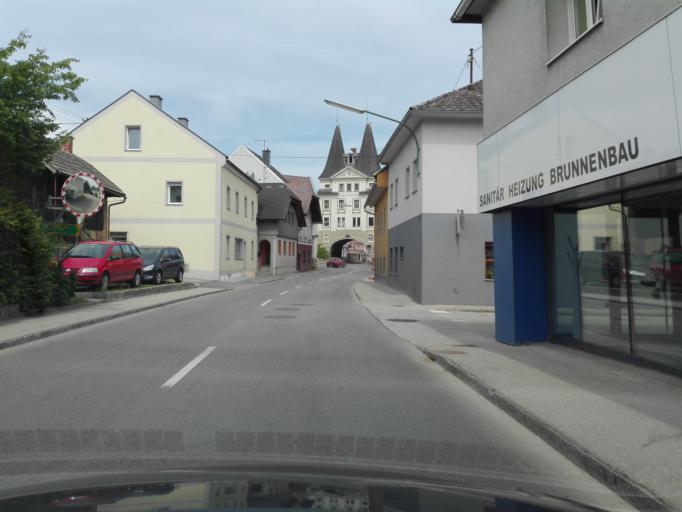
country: AT
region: Upper Austria
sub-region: Politischer Bezirk Vocklabruck
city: Schwanenstadt
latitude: 48.0535
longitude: 13.7714
